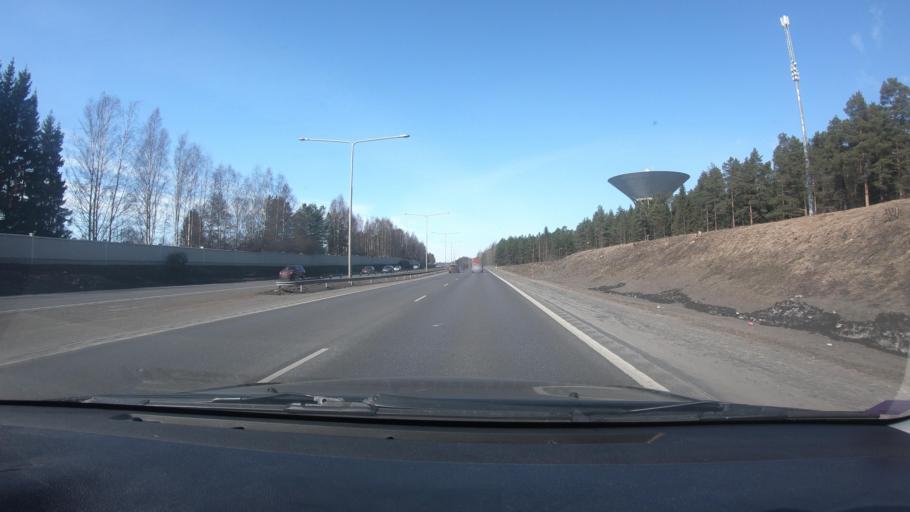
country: FI
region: Northern Ostrobothnia
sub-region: Oulu
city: Oulu
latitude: 65.0349
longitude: 25.4884
